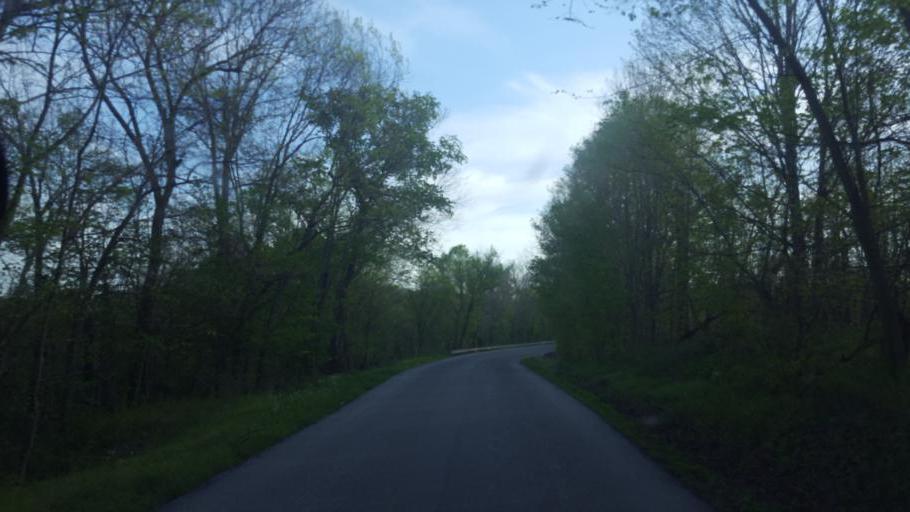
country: US
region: Kentucky
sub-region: Hart County
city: Munfordville
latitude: 37.2428
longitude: -85.9314
